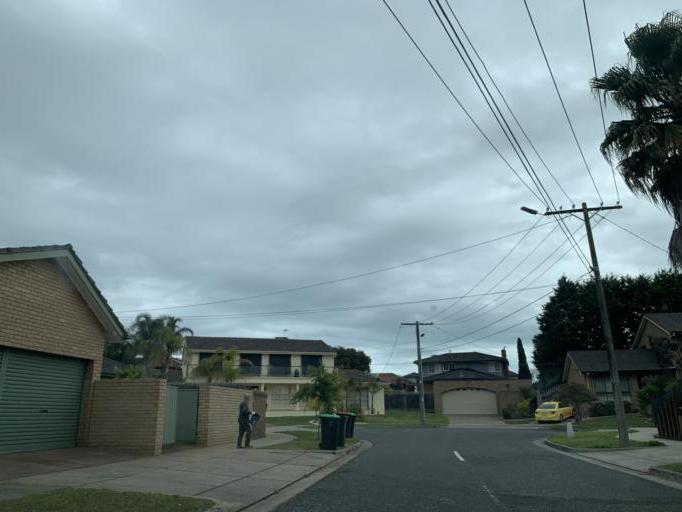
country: AU
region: Victoria
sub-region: Kingston
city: Mentone
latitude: -37.9774
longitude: 145.0770
